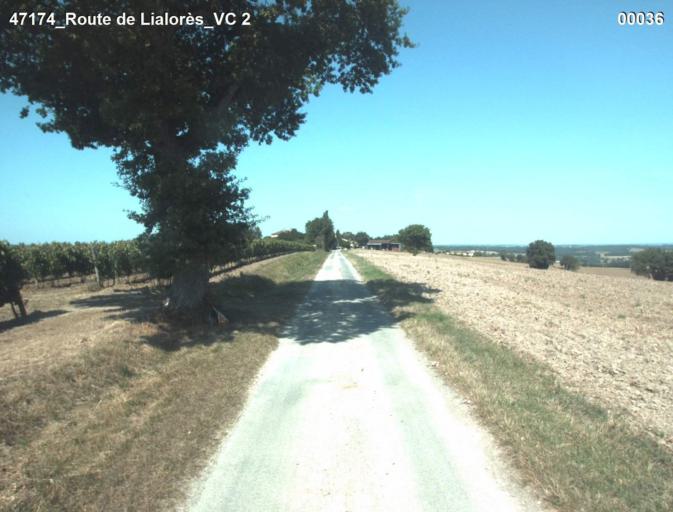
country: FR
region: Midi-Pyrenees
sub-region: Departement du Gers
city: Condom
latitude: 44.0090
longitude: 0.3841
